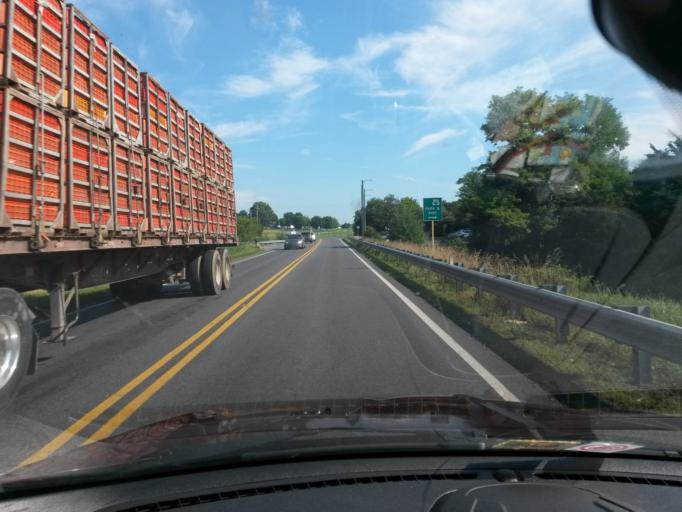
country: US
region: Virginia
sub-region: Rockingham County
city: Broadway
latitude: 38.5641
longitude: -78.7465
